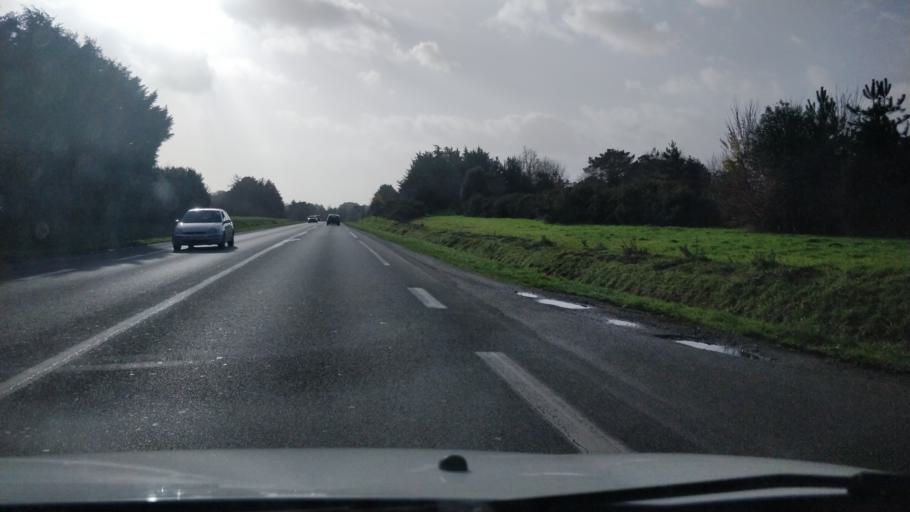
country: FR
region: Pays de la Loire
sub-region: Departement de la Loire-Atlantique
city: Guerande
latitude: 47.3238
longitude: -2.4151
